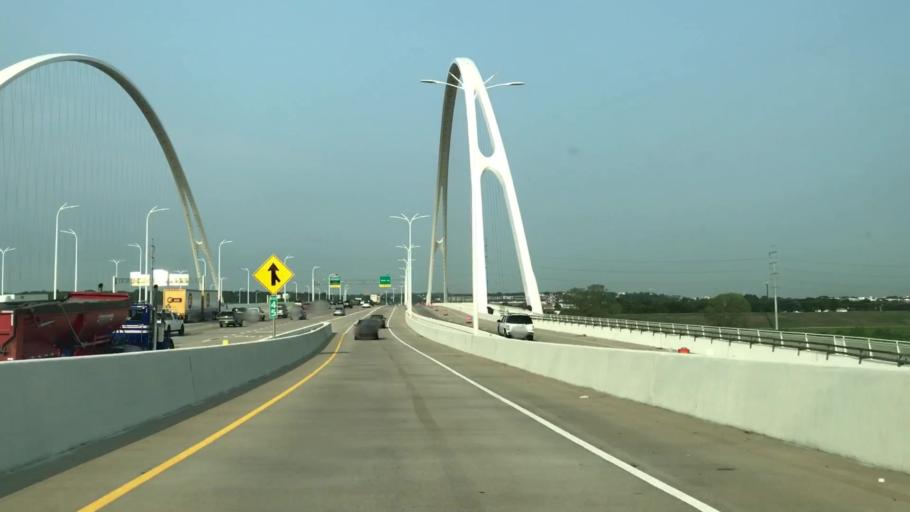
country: US
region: Texas
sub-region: Dallas County
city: Dallas
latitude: 32.7717
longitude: -96.8140
